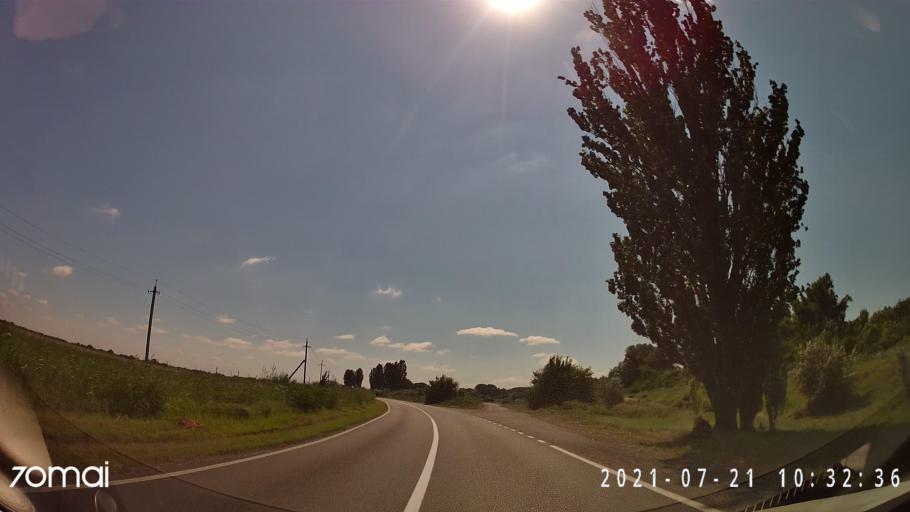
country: RO
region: Tulcea
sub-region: Oras Isaccea
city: Isaccea
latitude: 45.3006
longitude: 28.4272
